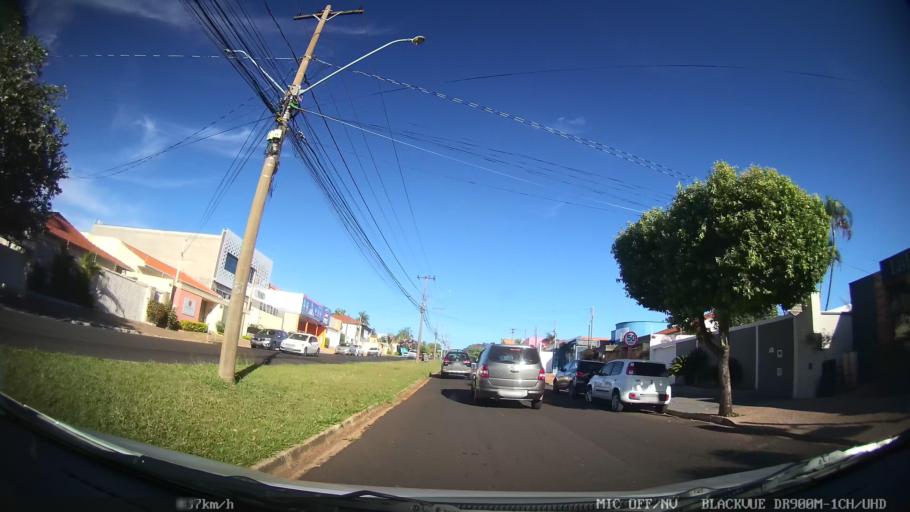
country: BR
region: Sao Paulo
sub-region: Araraquara
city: Araraquara
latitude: -21.7637
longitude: -48.1745
